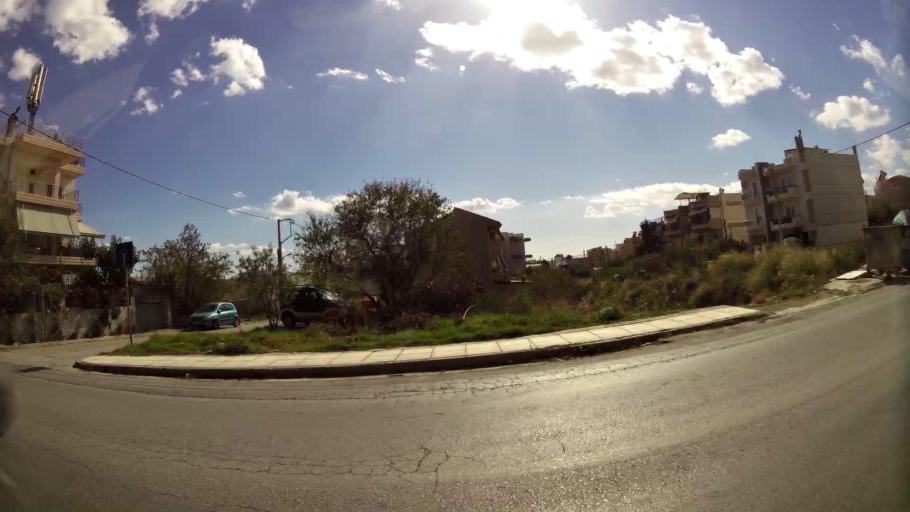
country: GR
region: Attica
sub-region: Nomarchia Anatolikis Attikis
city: Acharnes
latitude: 38.0976
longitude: 23.7369
